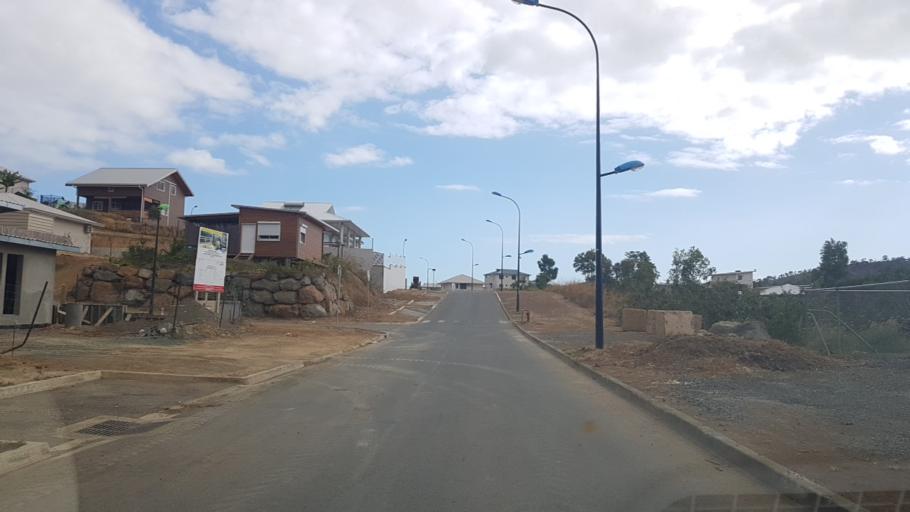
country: NC
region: South Province
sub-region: Dumbea
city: Dumbea
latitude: -22.1982
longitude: 166.4422
